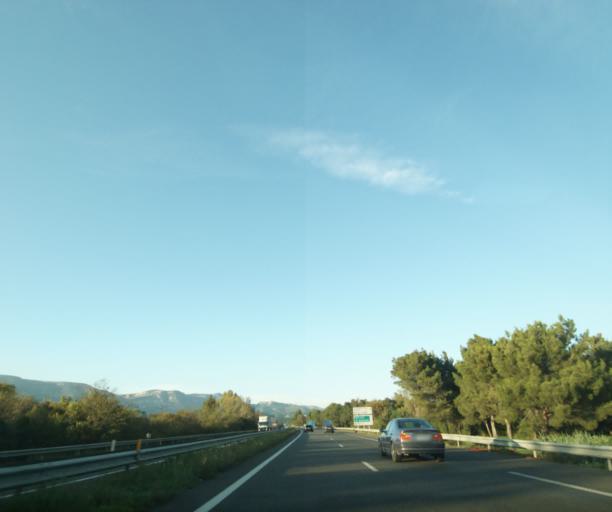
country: FR
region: Provence-Alpes-Cote d'Azur
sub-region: Departement des Bouches-du-Rhone
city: Aubagne
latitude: 43.3079
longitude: 5.5921
